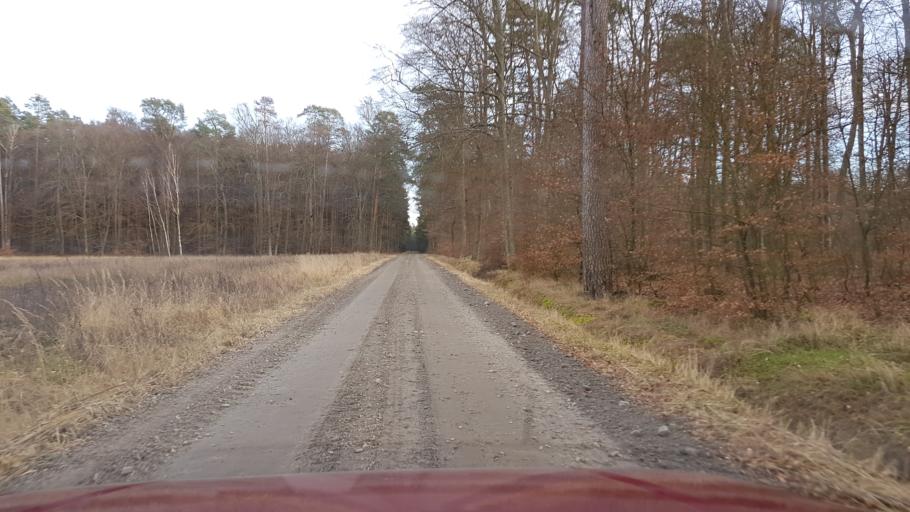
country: PL
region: Lubusz
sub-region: Powiat strzelecko-drezdenecki
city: Strzelce Krajenskie
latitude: 52.9098
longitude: 15.3854
